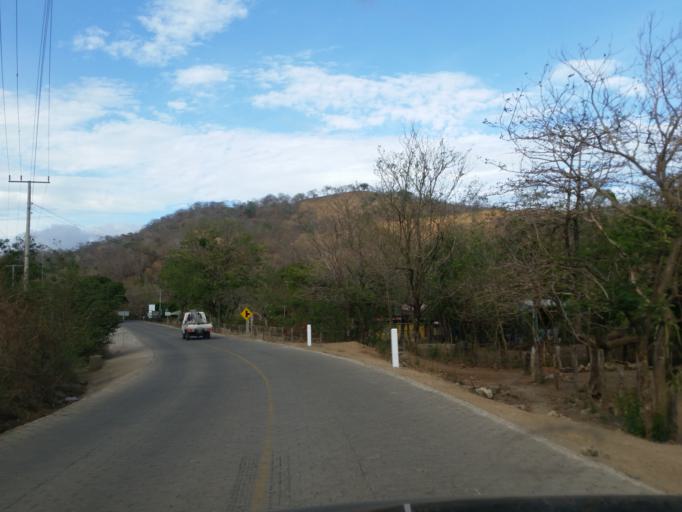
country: NI
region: Rivas
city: Tola
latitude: 11.3921
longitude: -85.9624
